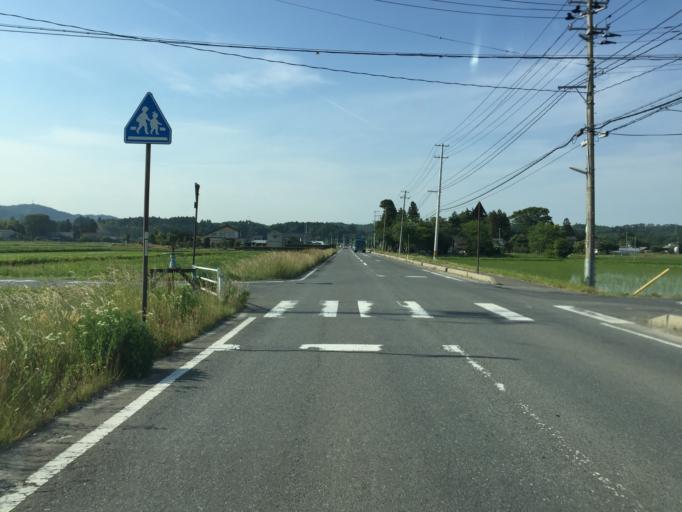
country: JP
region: Fukushima
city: Namie
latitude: 37.6625
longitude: 140.9329
